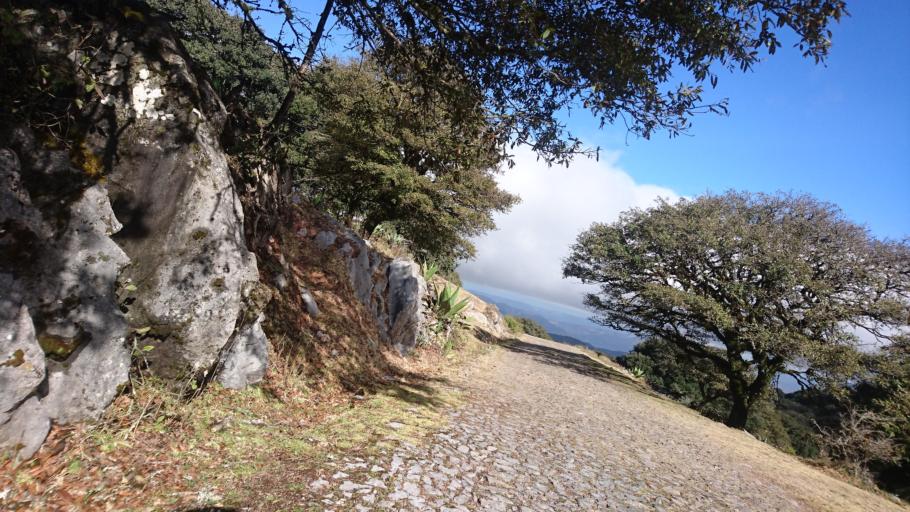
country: MX
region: San Luis Potosi
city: Zaragoza
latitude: 22.0655
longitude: -100.6410
